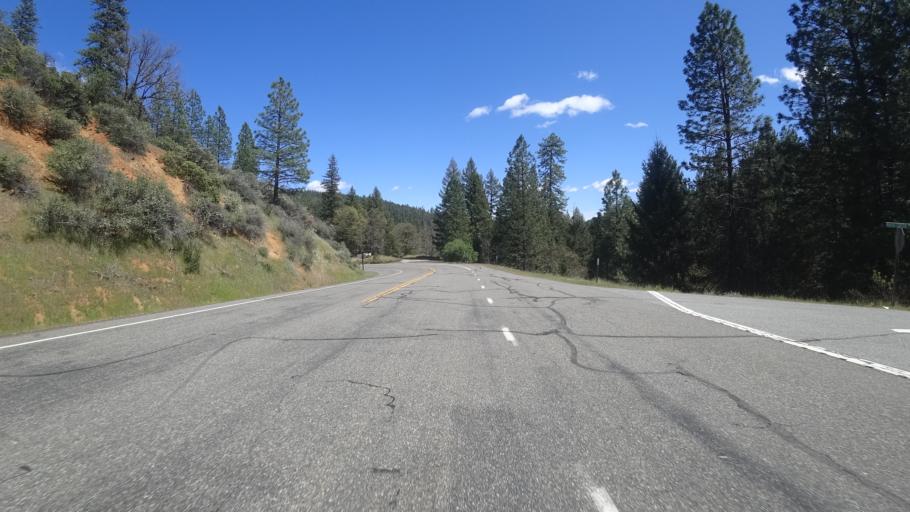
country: US
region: California
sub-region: Trinity County
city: Weaverville
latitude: 40.7953
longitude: -122.8906
